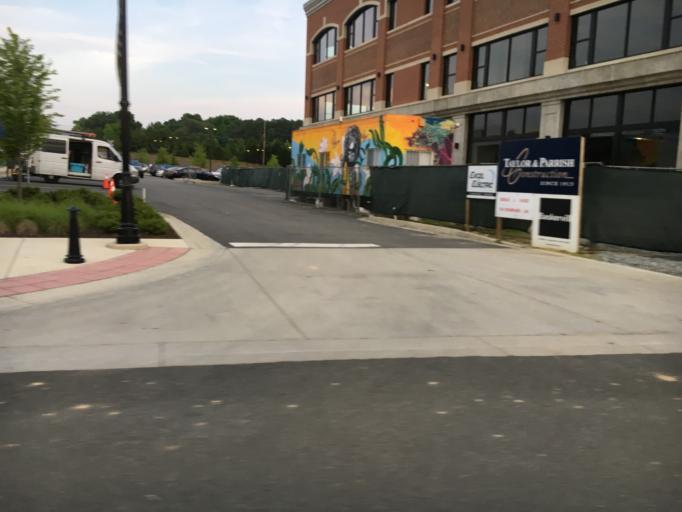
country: US
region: Virginia
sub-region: Henrico County
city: Short Pump
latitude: 37.6585
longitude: -77.6370
